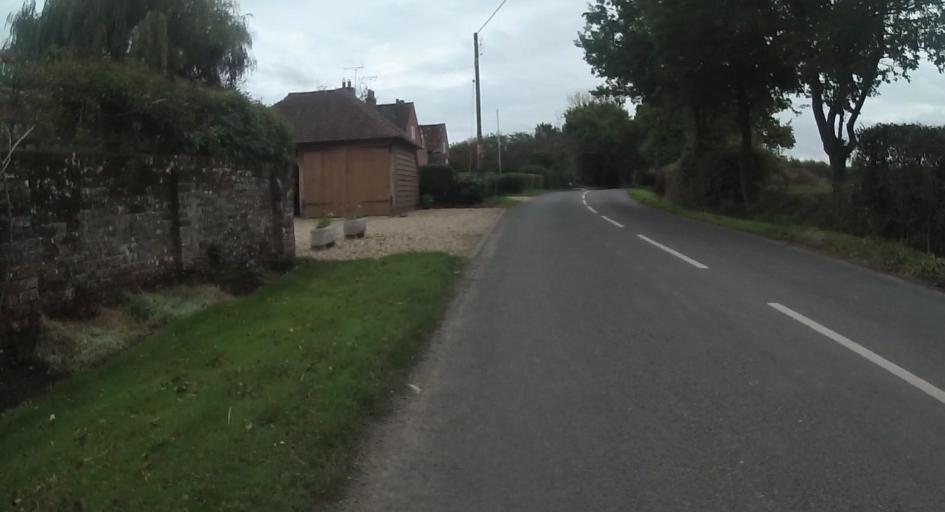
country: GB
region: England
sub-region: Hampshire
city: Odiham
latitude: 51.2839
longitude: -0.9014
